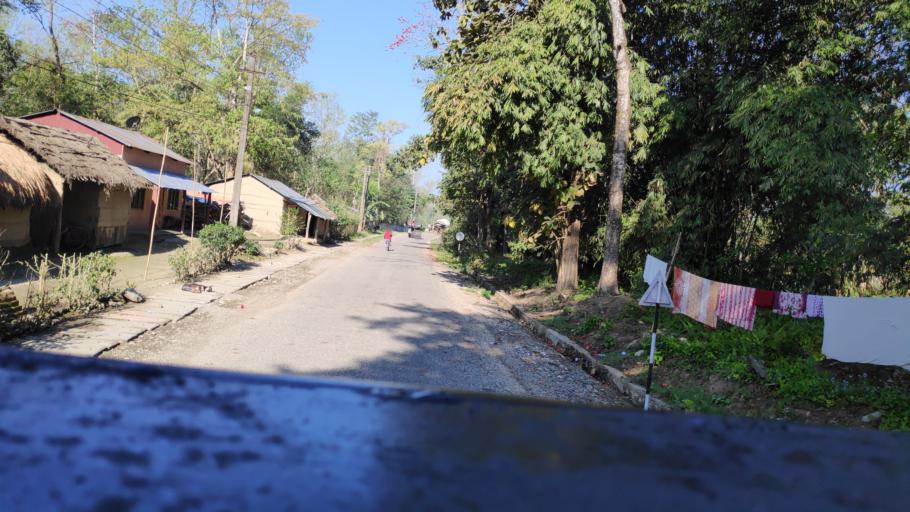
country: NP
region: Central Region
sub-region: Narayani Zone
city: Bharatpur
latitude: 27.5738
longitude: 84.5095
